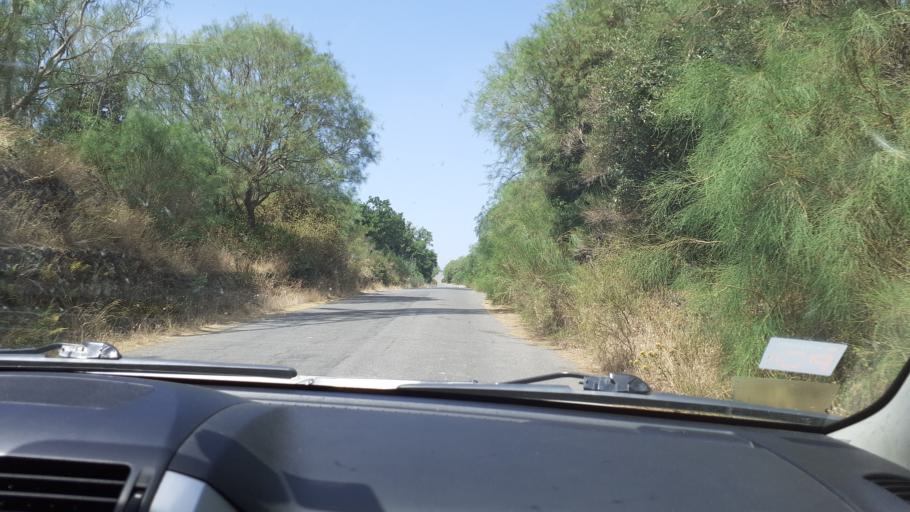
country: IT
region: Sicily
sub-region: Catania
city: Nicolosi
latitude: 37.6471
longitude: 15.0155
